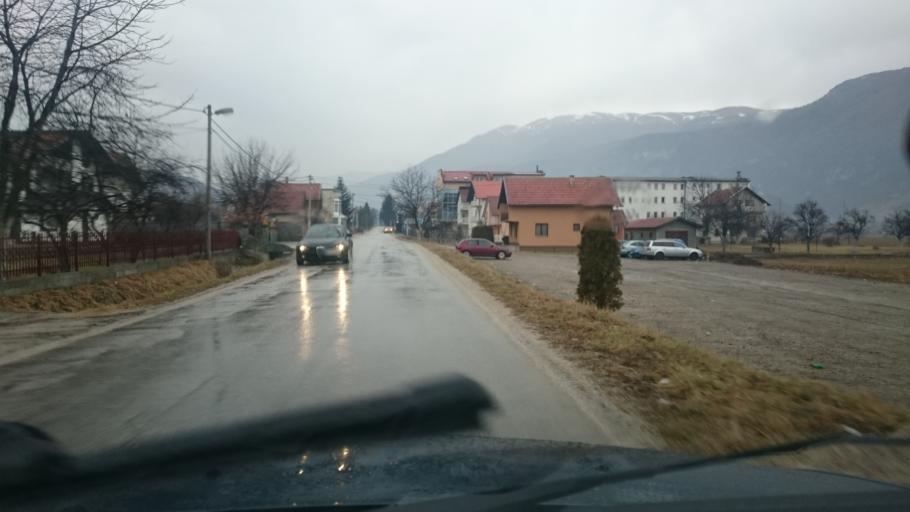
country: BA
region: Federation of Bosnia and Herzegovina
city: Travnik
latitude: 44.2090
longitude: 17.6942
